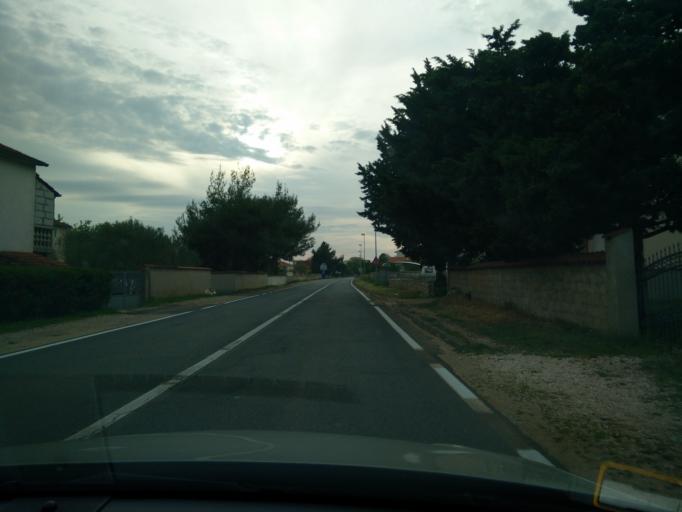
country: HR
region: Zadarska
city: Turanj
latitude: 43.9661
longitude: 15.4158
